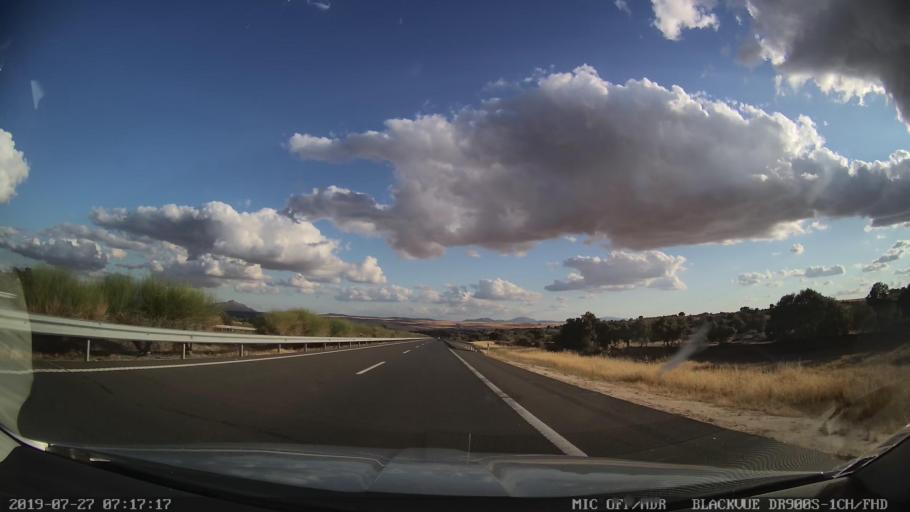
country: ES
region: Extremadura
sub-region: Provincia de Caceres
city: Trujillo
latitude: 39.4416
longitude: -5.8756
